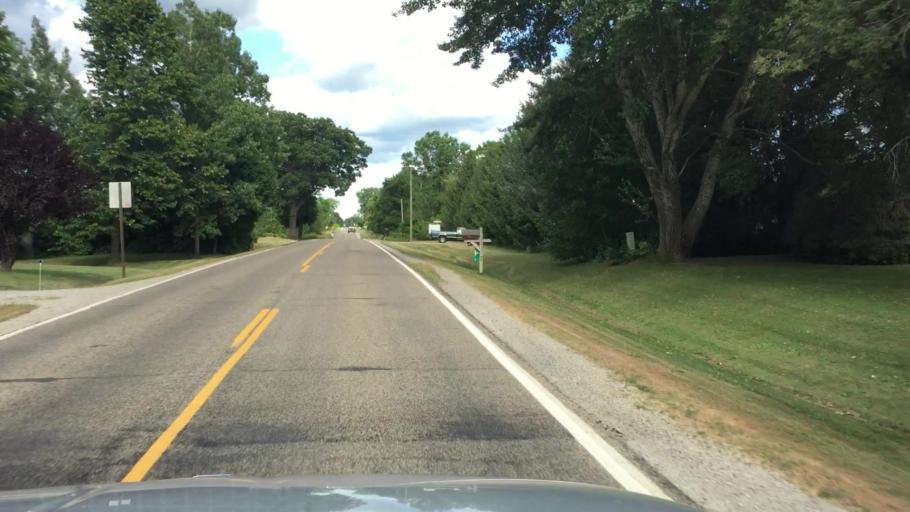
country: US
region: Michigan
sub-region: Saint Clair County
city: Yale
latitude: 43.1285
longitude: -82.8535
